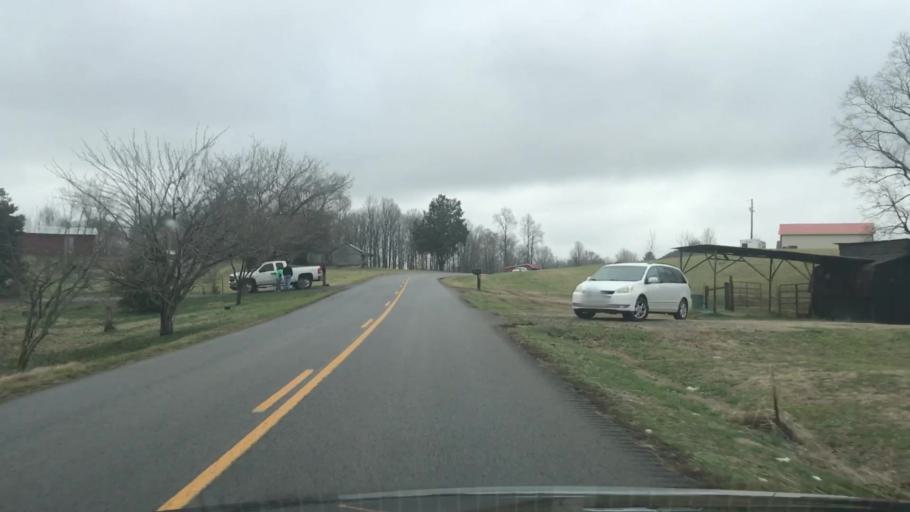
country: US
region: Kentucky
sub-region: Monroe County
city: Tompkinsville
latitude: 36.7857
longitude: -85.7394
